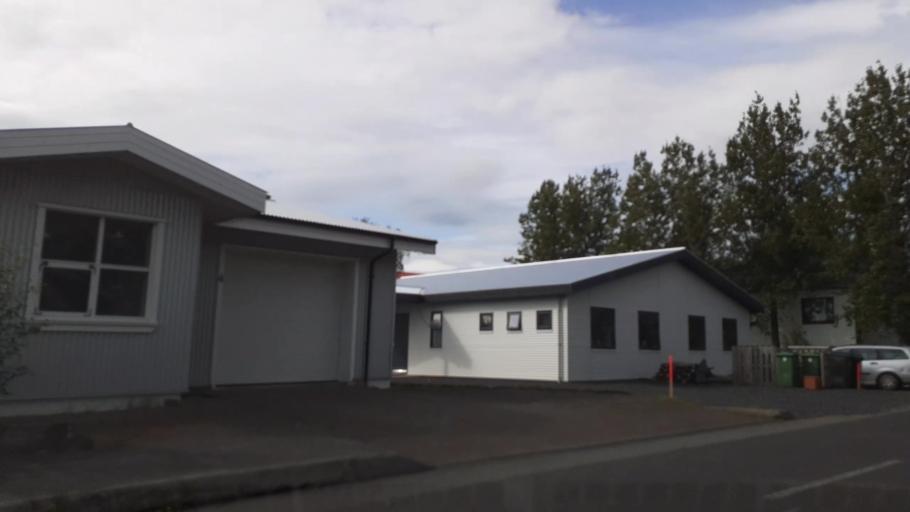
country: IS
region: South
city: Vestmannaeyjar
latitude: 63.8384
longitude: -20.3995
